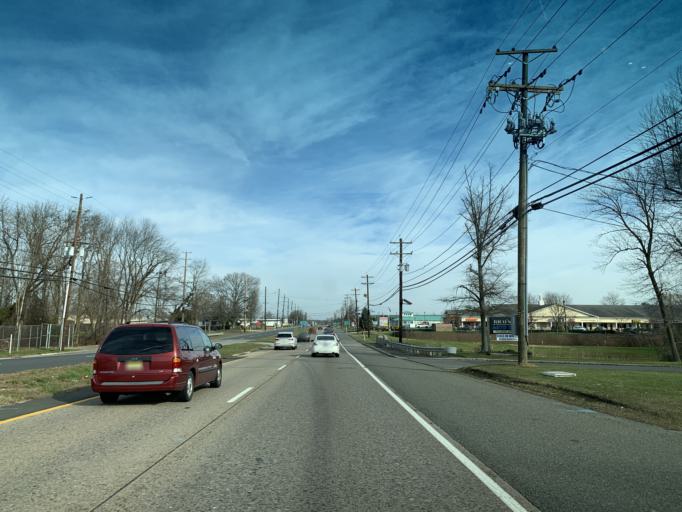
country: US
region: New Jersey
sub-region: Mercer County
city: Yardville
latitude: 40.1887
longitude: -74.6530
